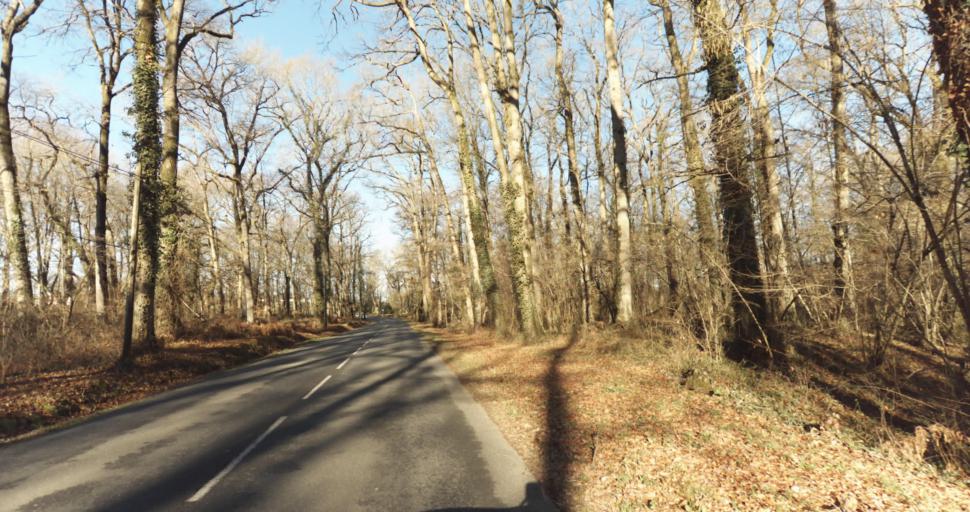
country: FR
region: Aquitaine
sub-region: Departement des Pyrenees-Atlantiques
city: Morlaas
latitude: 43.3386
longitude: -0.2450
